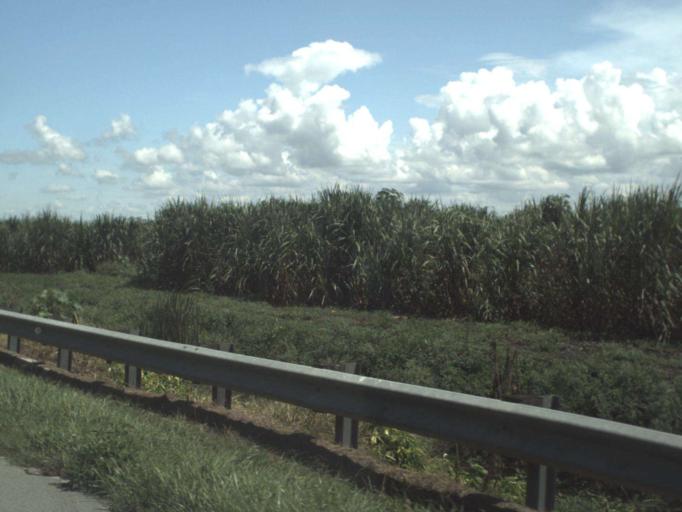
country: US
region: Florida
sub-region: Palm Beach County
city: Pahokee
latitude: 26.8529
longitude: -80.6380
